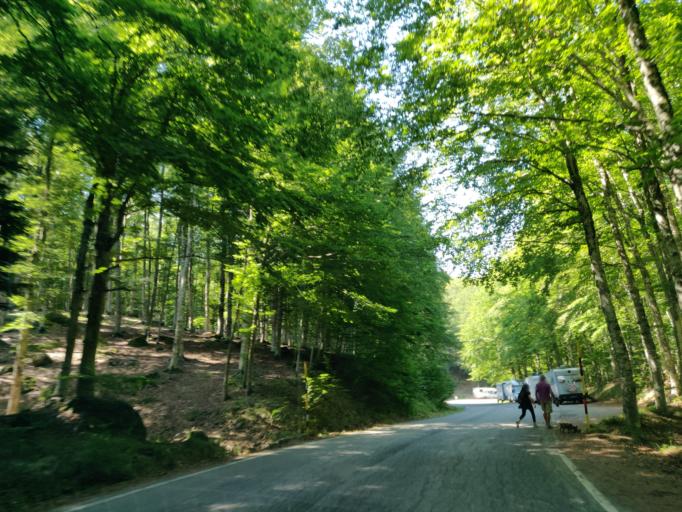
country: IT
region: Tuscany
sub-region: Provincia di Siena
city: Abbadia San Salvatore
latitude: 42.8913
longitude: 11.6110
